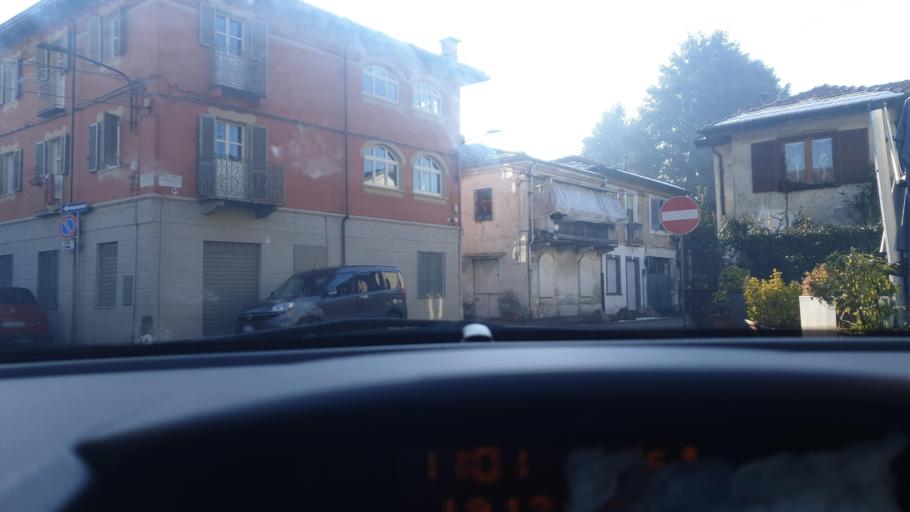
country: IT
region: Piedmont
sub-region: Provincia di Torino
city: San Mauro Torinese
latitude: 45.1005
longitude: 7.7456
